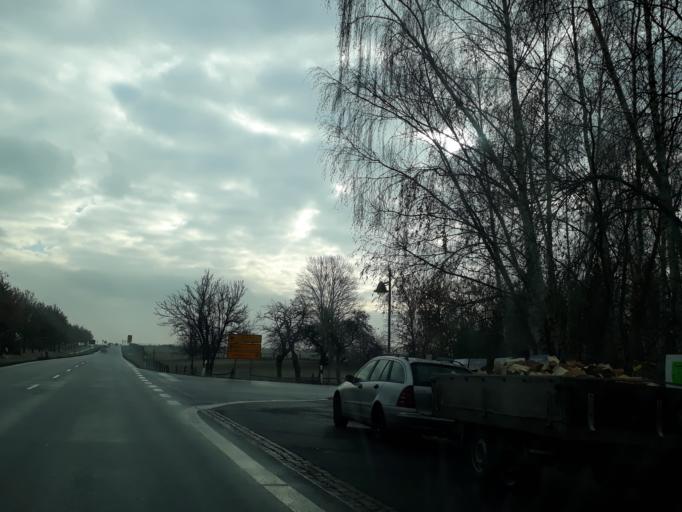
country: DE
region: Saxony
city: Lobau
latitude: 51.1171
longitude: 14.6441
